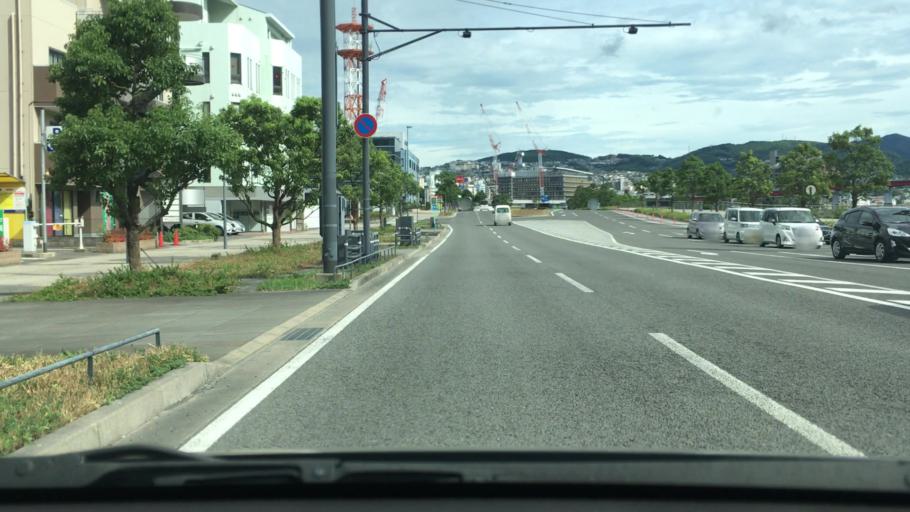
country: JP
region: Nagasaki
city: Nagasaki-shi
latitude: 32.7568
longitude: 129.8654
